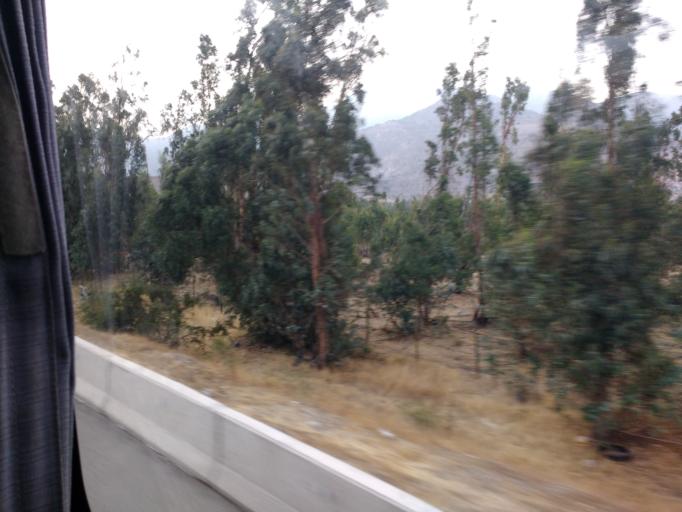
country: CL
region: Santiago Metropolitan
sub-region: Provincia de Talagante
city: Penaflor
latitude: -33.4578
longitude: -70.9118
